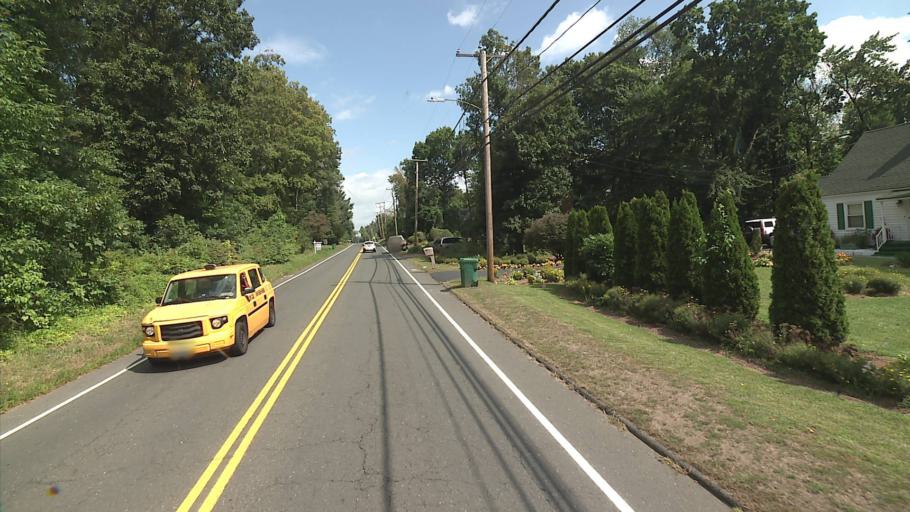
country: US
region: Connecticut
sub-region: Hartford County
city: Blue Hills
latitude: 41.8212
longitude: -72.7383
